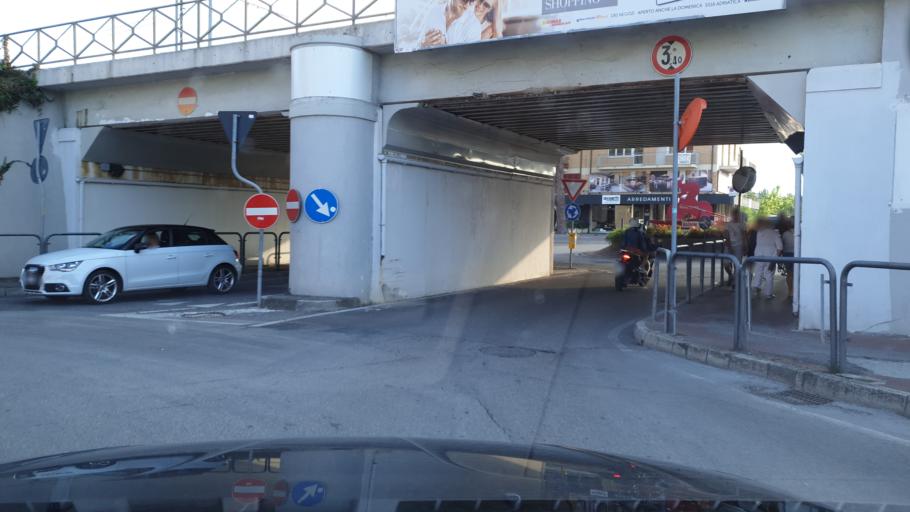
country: IT
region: Emilia-Romagna
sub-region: Provincia di Rimini
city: Riccione
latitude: 44.0034
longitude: 12.6540
